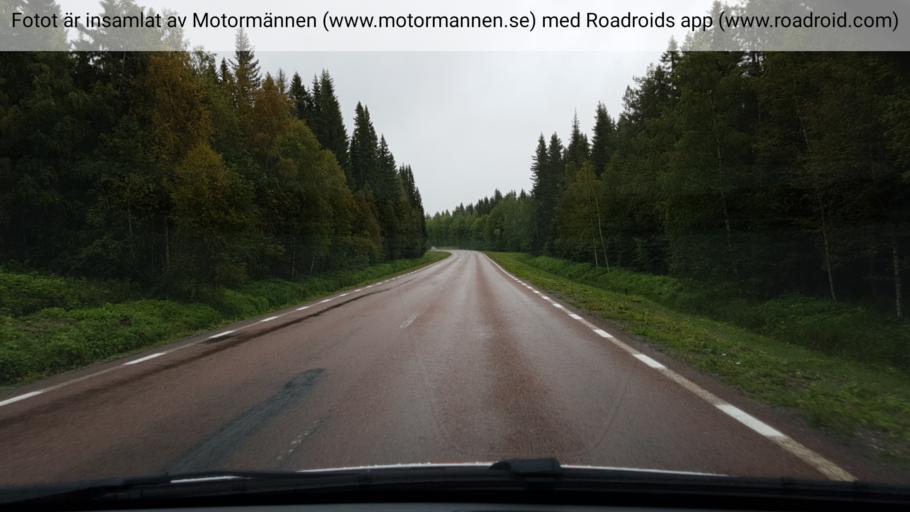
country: SE
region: Jaemtland
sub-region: Stroemsunds Kommun
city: Stroemsund
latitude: 63.8812
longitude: 15.6673
